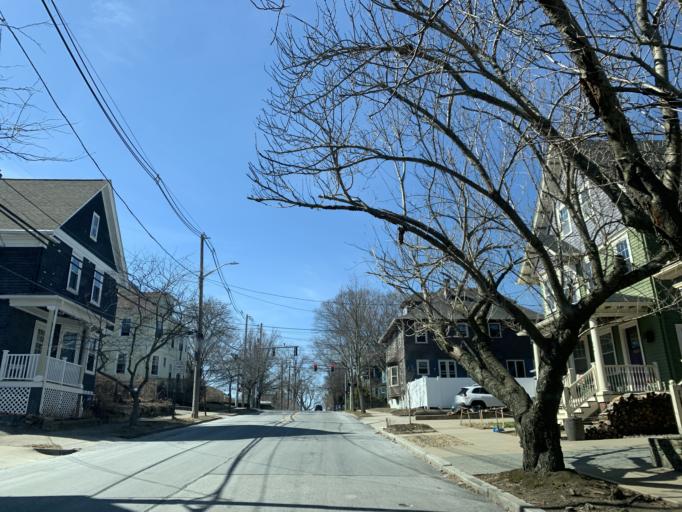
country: US
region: Rhode Island
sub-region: Providence County
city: Providence
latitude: 41.8408
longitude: -71.3982
